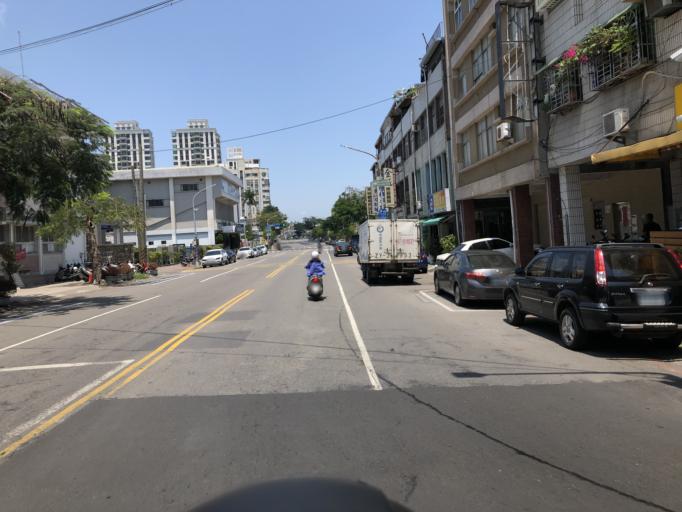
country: TW
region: Kaohsiung
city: Kaohsiung
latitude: 22.6264
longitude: 120.2782
